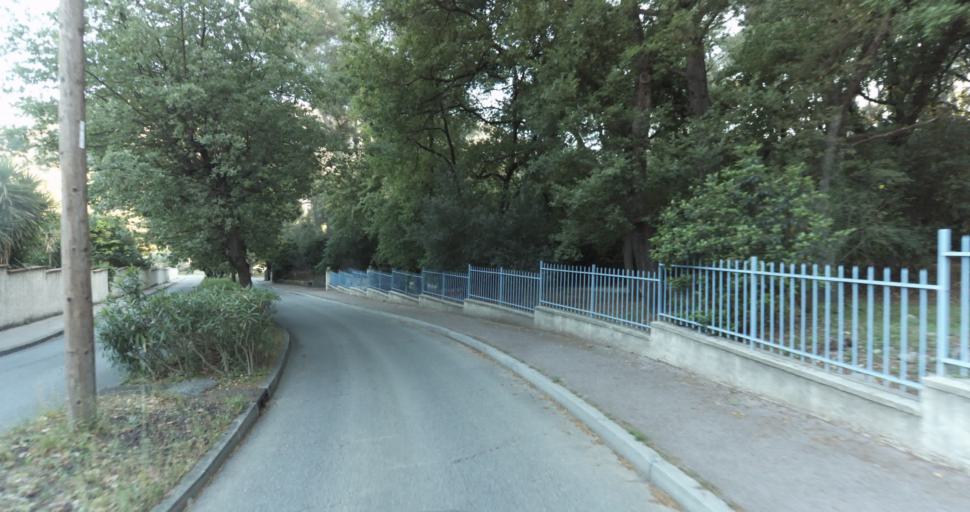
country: FR
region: Provence-Alpes-Cote d'Azur
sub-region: Departement du Var
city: Le Revest-les-Eaux
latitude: 43.1666
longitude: 5.9369
